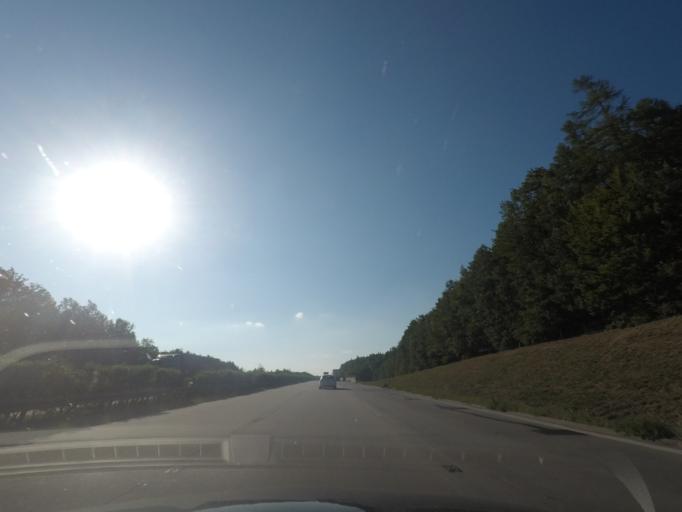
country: CZ
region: Olomoucky
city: Dolni Ujezd
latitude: 49.5576
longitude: 17.5200
